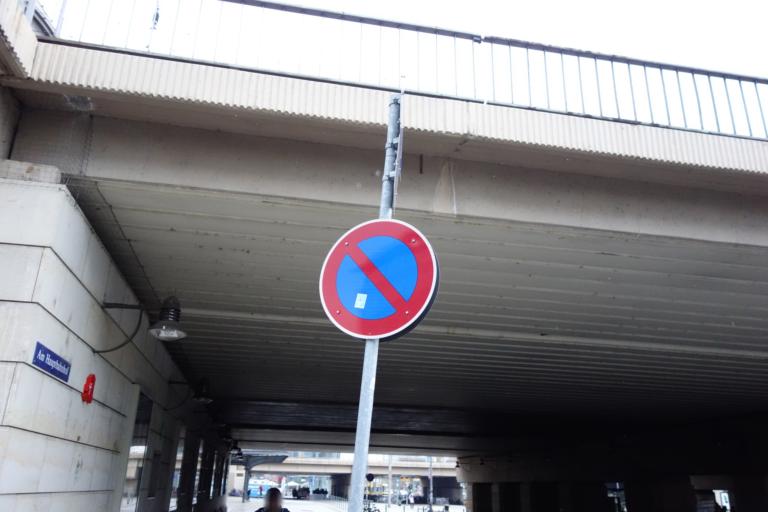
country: DE
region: Saxony
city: Dresden
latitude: 51.0391
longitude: 13.7324
